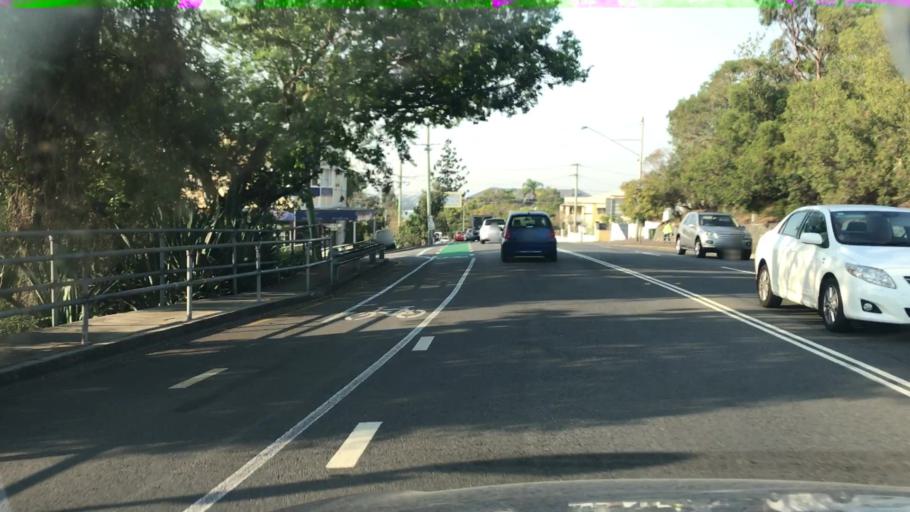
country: AU
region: Queensland
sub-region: Brisbane
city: South Brisbane
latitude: -27.4883
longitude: 153.0187
